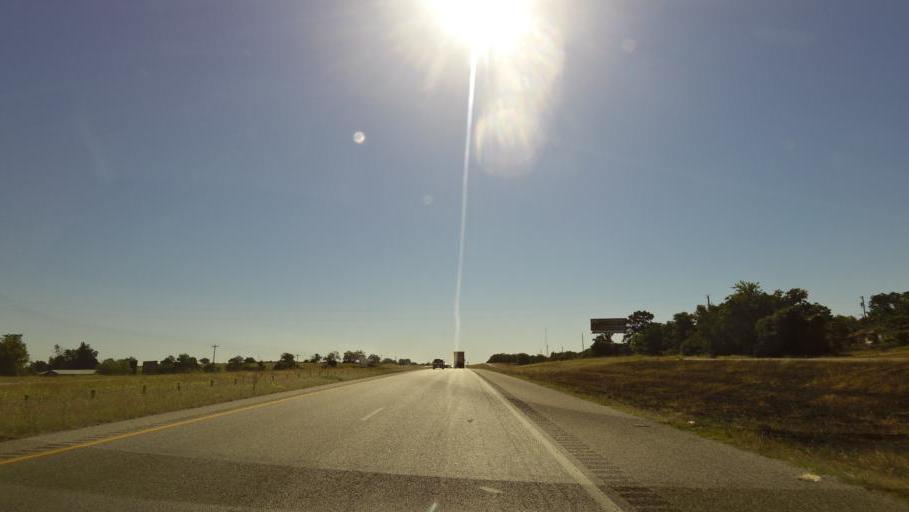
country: US
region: Texas
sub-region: Caldwell County
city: Luling
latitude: 29.6540
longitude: -97.5733
